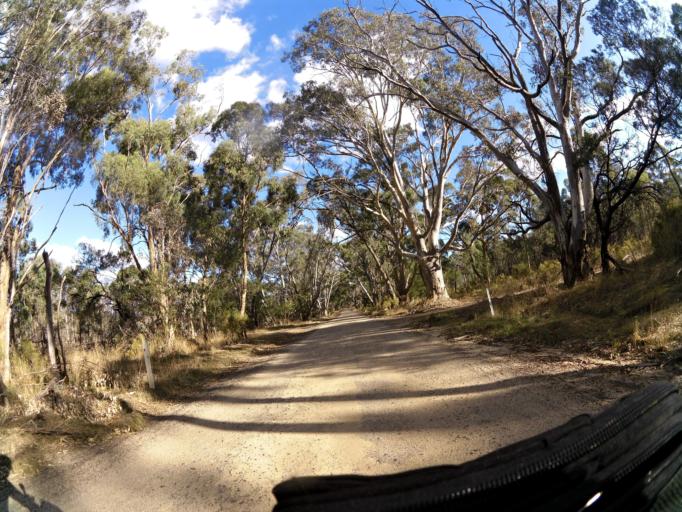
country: AU
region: Victoria
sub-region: Greater Bendigo
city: Kennington
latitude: -37.0091
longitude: 144.8097
